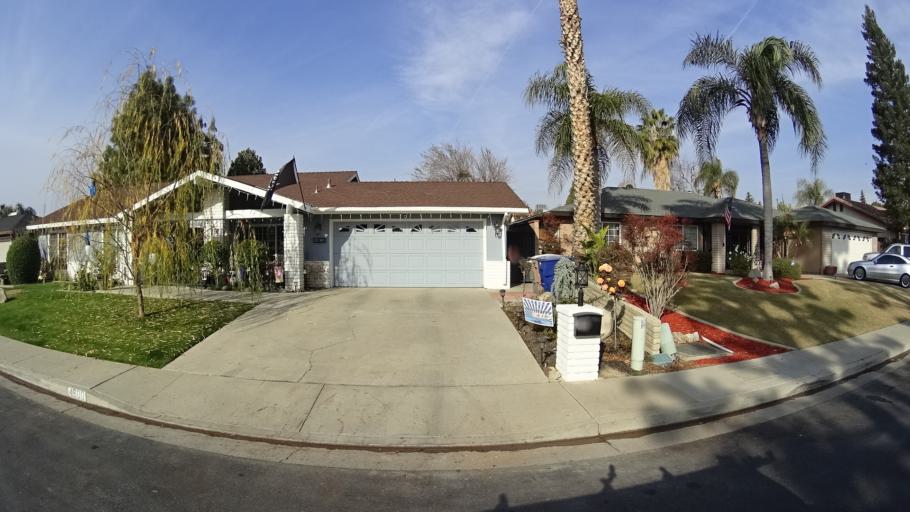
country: US
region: California
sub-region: Kern County
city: Oildale
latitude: 35.4084
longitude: -118.9421
